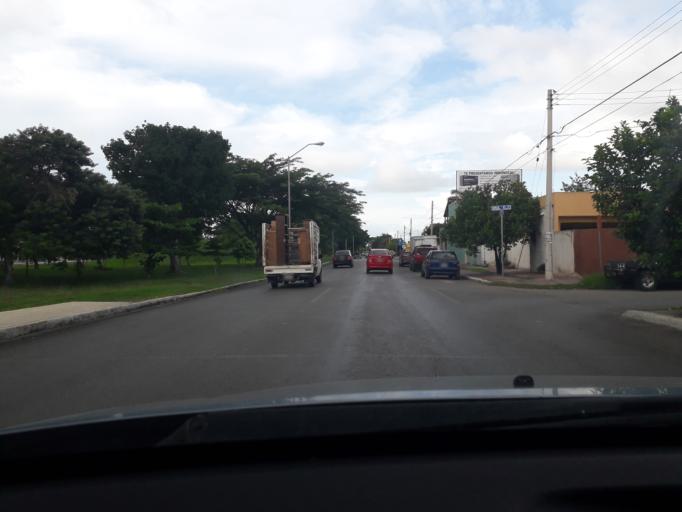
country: MX
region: Yucatan
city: Merida
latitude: 20.9797
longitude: -89.6633
